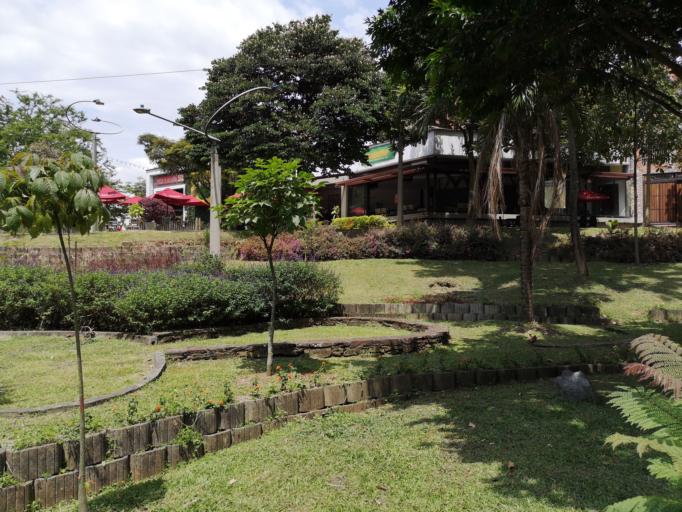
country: CO
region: Antioquia
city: Itagui
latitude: 6.2082
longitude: -75.5708
